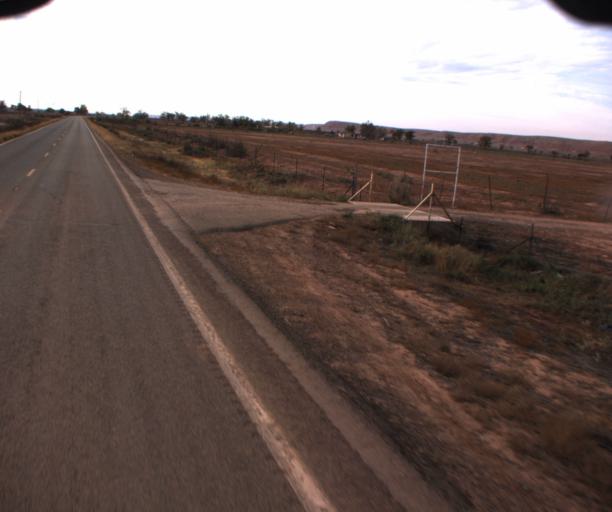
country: US
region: Arizona
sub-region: Apache County
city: Many Farms
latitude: 36.4271
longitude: -109.6066
